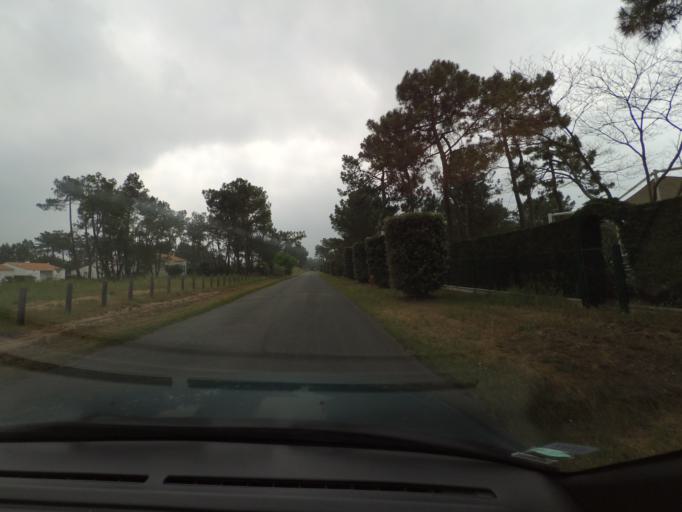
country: FR
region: Poitou-Charentes
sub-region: Departement de la Charente-Maritime
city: Saint-Martin-de-Re
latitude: 46.3130
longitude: -1.3052
